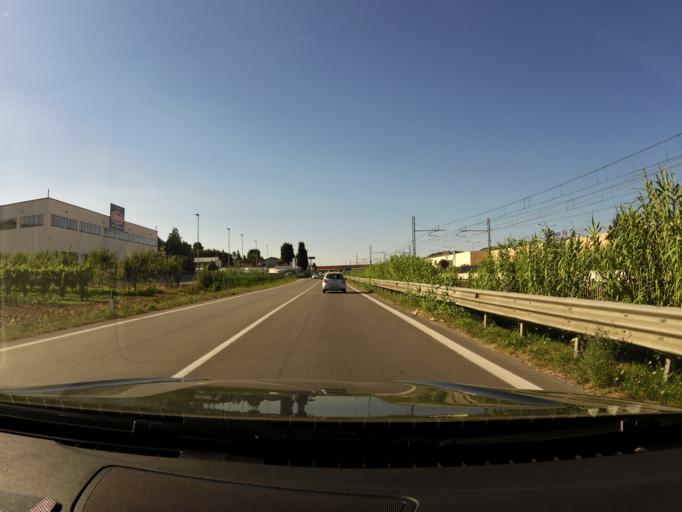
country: IT
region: The Marches
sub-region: Provincia di Ancona
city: San Biagio
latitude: 43.5199
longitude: 13.5248
